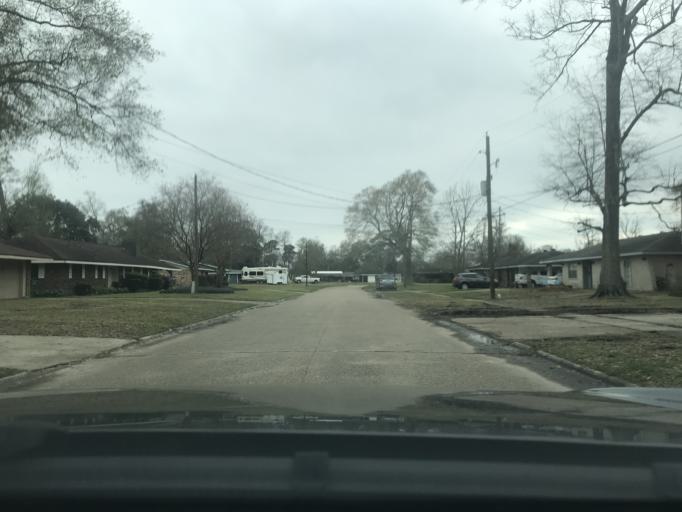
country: US
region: Louisiana
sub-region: Calcasieu Parish
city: Westlake
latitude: 30.2540
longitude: -93.2555
